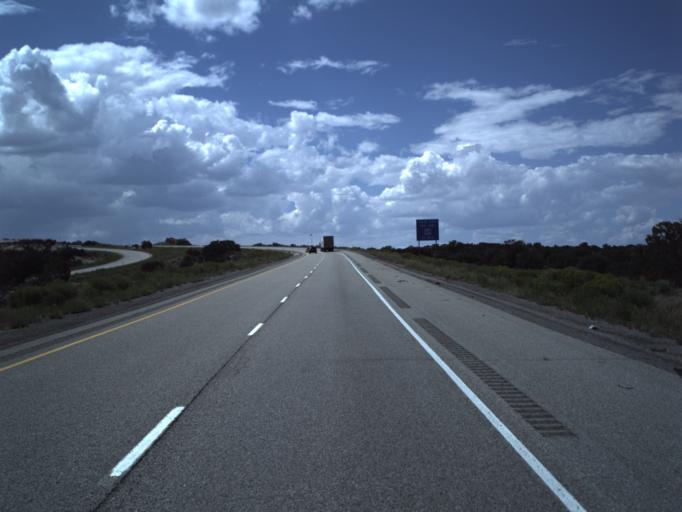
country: US
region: Utah
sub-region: Emery County
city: Ferron
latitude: 38.8658
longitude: -110.7995
